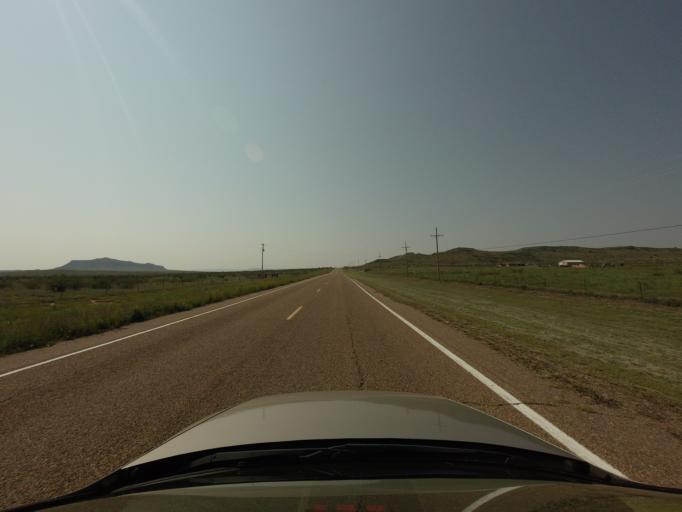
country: US
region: New Mexico
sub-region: Quay County
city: Tucumcari
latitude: 35.1207
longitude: -103.7287
